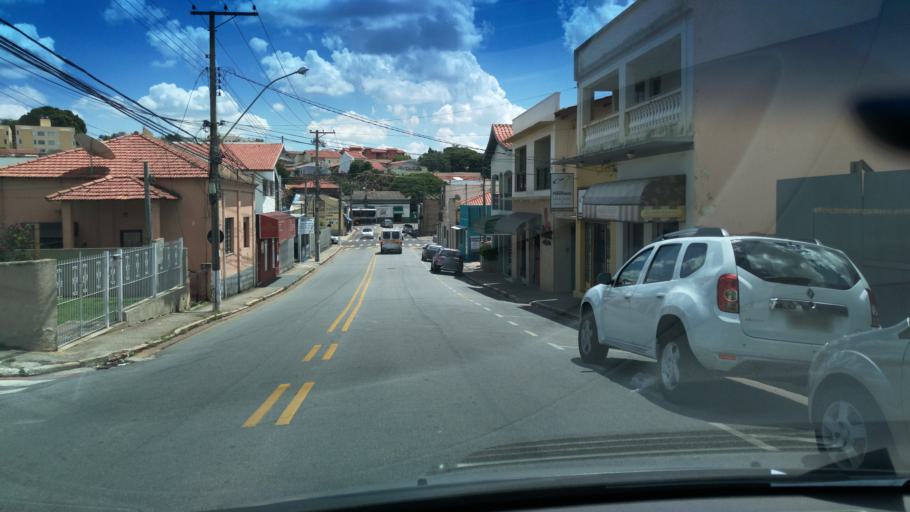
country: BR
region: Sao Paulo
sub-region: Vinhedo
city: Vinhedo
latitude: -23.0278
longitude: -46.9777
